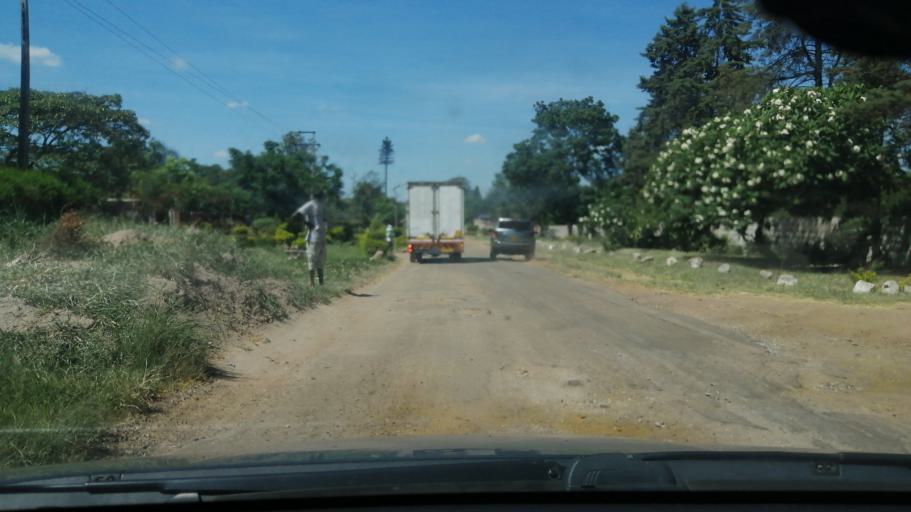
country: ZW
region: Harare
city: Epworth
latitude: -17.8200
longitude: 31.1298
